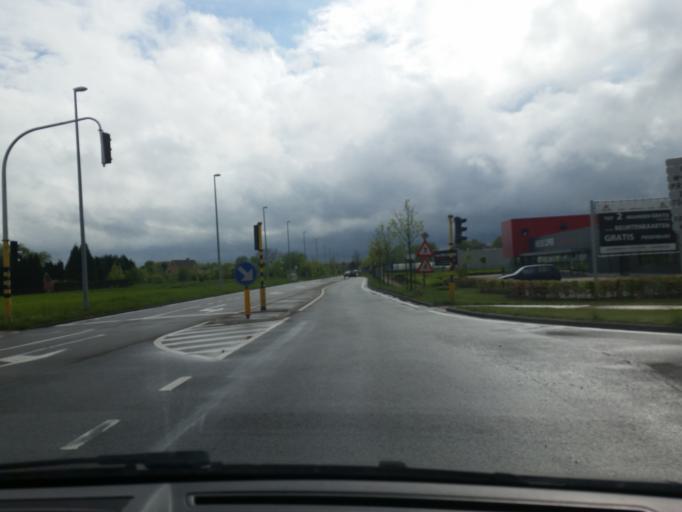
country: BE
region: Flanders
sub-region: Provincie Antwerpen
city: Lier
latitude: 51.1091
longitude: 4.5530
